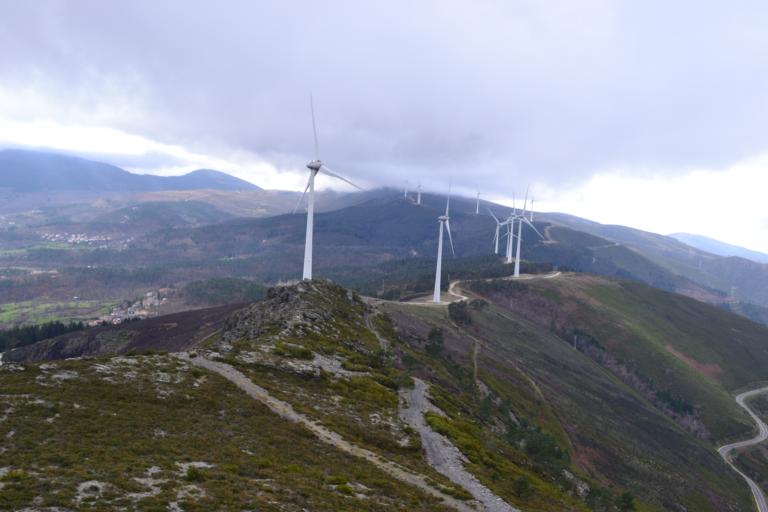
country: PT
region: Vila Real
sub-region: Mondim de Basto
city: Mondim de Basto
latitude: 41.3263
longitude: -7.8693
